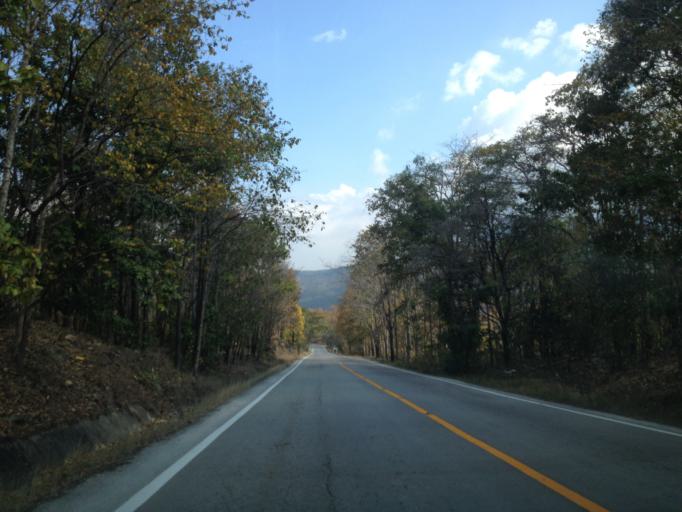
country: TH
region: Chiang Mai
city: Hot
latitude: 18.1656
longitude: 98.4405
